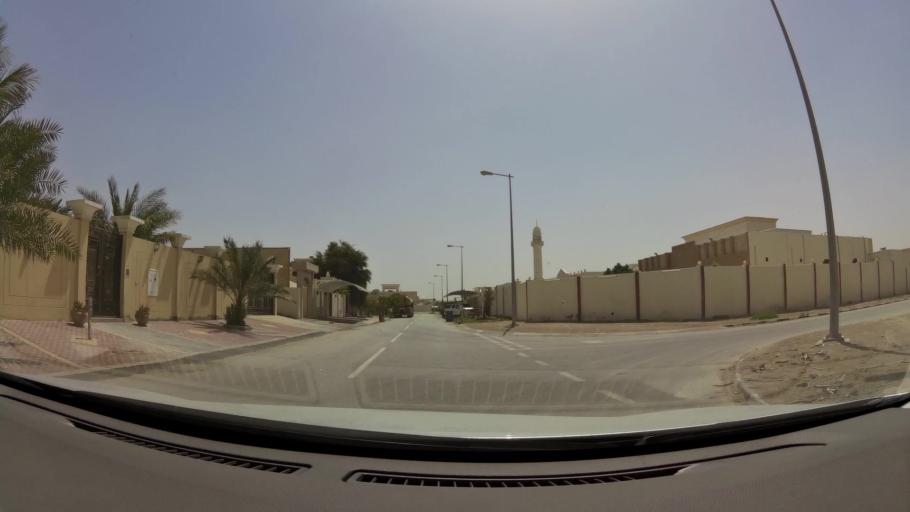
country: QA
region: Baladiyat Umm Salal
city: Umm Salal Muhammad
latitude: 25.4021
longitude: 51.4350
